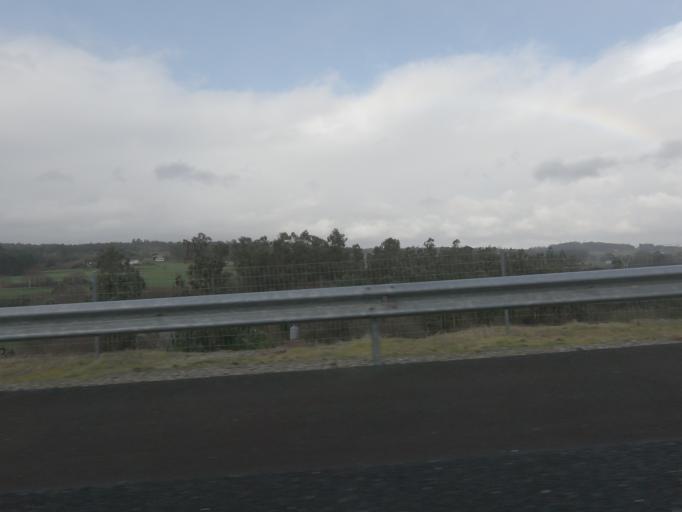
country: ES
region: Galicia
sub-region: Provincia da Coruna
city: Ribeira
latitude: 42.7451
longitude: -8.3767
